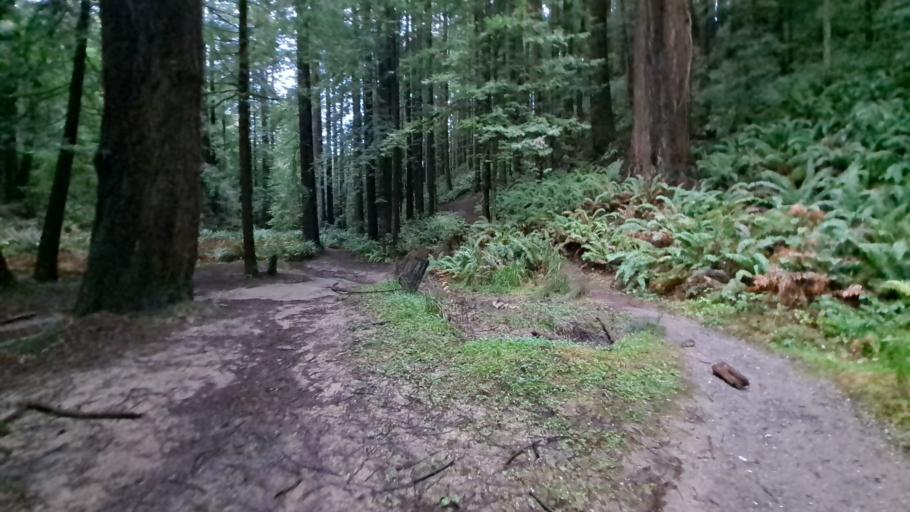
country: US
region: California
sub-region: Humboldt County
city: Fortuna
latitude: 40.6024
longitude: -124.1472
